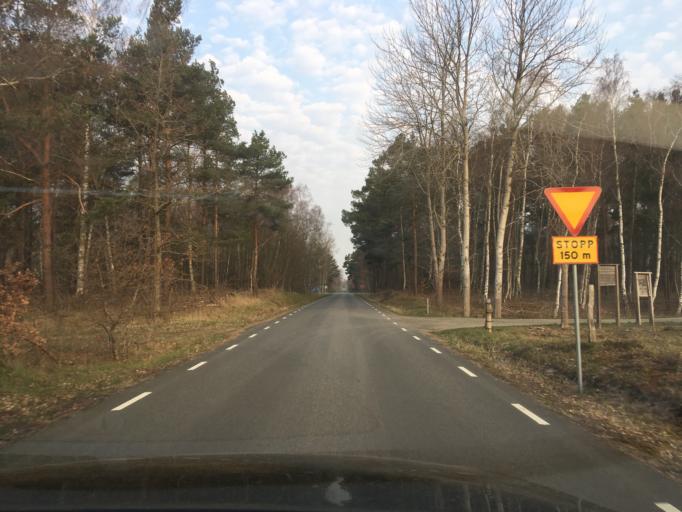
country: SE
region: Skane
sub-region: Simrishamns Kommun
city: Simrishamn
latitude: 55.3942
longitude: 14.1794
